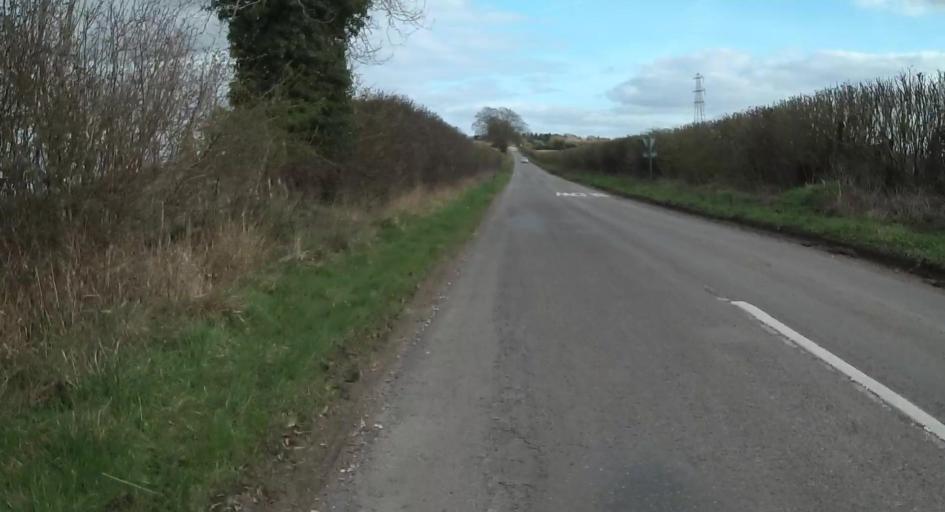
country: GB
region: England
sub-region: Hampshire
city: Andover
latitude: 51.1606
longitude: -1.4863
